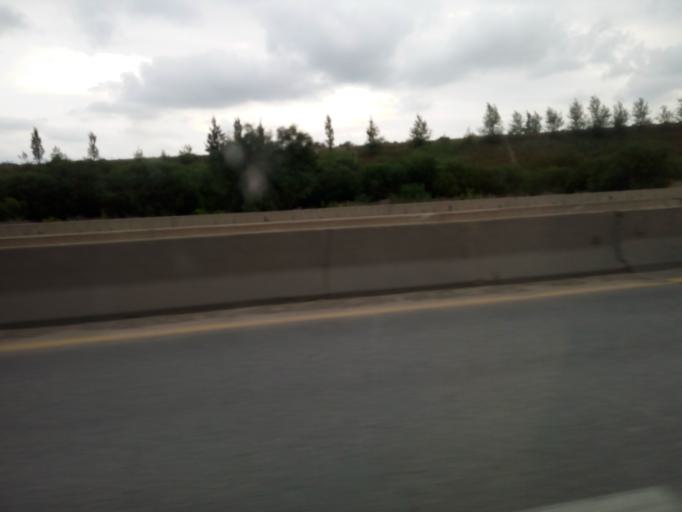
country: DZ
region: Tipaza
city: Saoula
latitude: 36.6469
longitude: 3.0247
